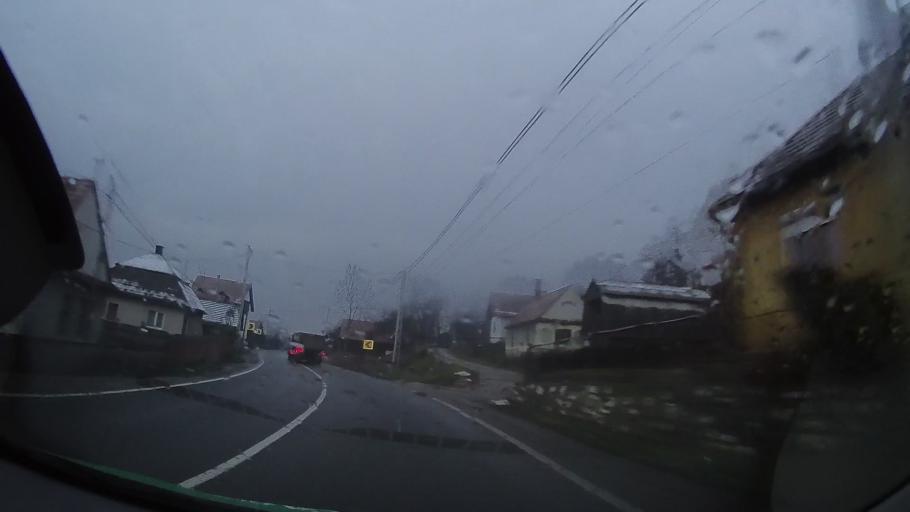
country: RO
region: Harghita
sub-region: Comuna Lazarea
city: Lazarea
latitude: 46.7522
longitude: 25.5199
